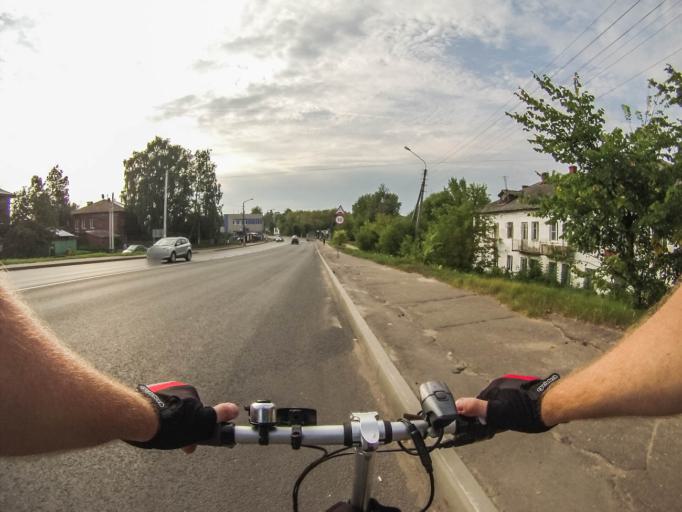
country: RU
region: Kostroma
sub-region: Kostromskoy Rayon
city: Kostroma
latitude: 57.7815
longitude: 40.8923
